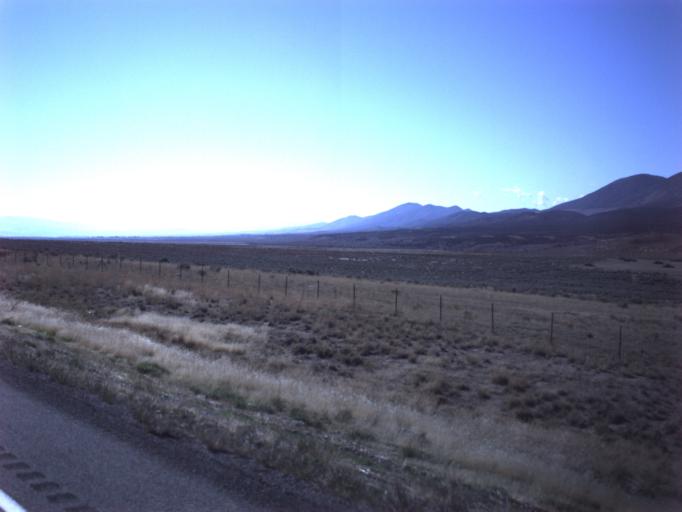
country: US
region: Utah
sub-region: Sanpete County
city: Gunnison
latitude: 39.3262
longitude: -111.9113
